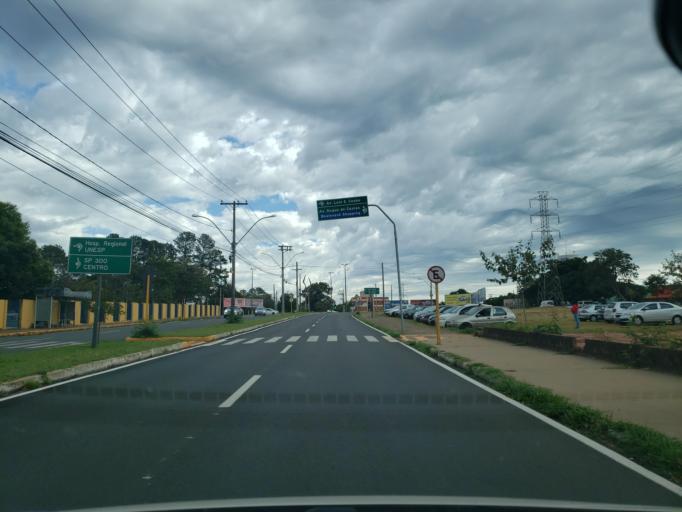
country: BR
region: Sao Paulo
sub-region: Bauru
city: Bauru
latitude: -22.3379
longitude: -49.0275
